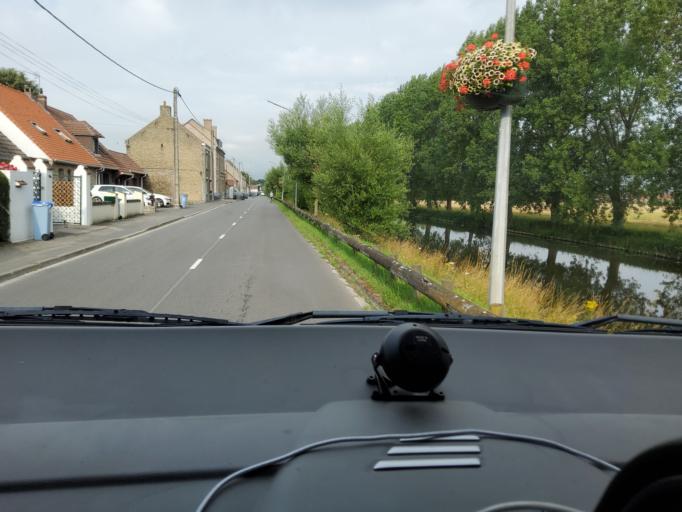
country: FR
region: Nord-Pas-de-Calais
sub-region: Departement du Nord
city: Bourbourg
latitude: 50.9485
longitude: 2.2076
